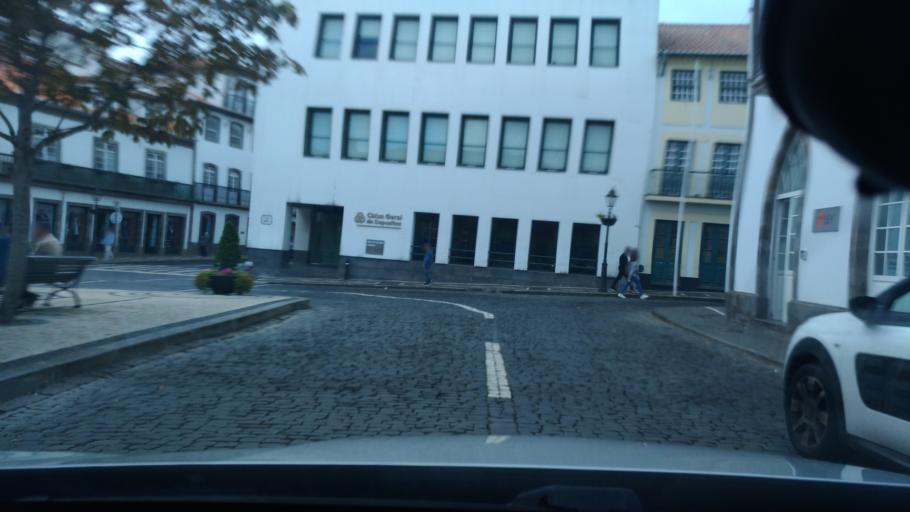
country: PT
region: Azores
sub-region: Angra do Heroismo
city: Angra do Heroismo
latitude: 38.6561
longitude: -27.2188
